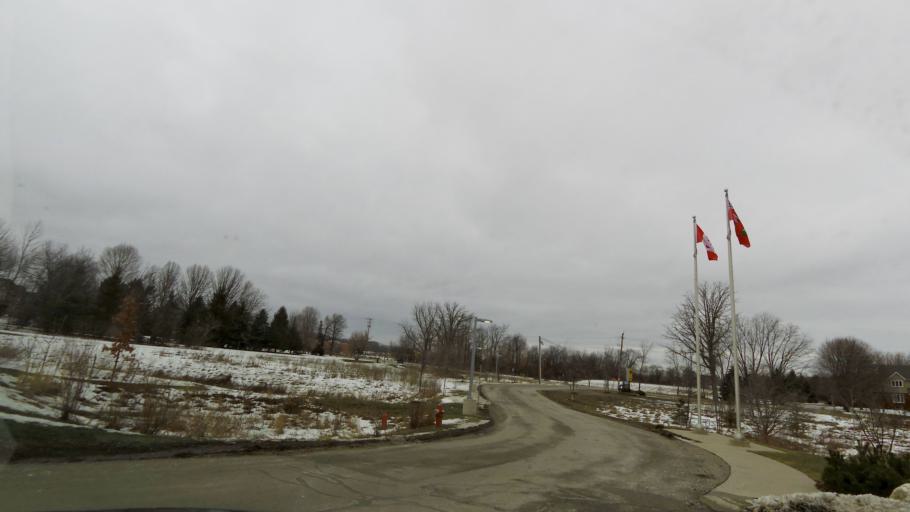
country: CA
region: Ontario
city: Brampton
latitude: 43.8765
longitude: -79.8536
